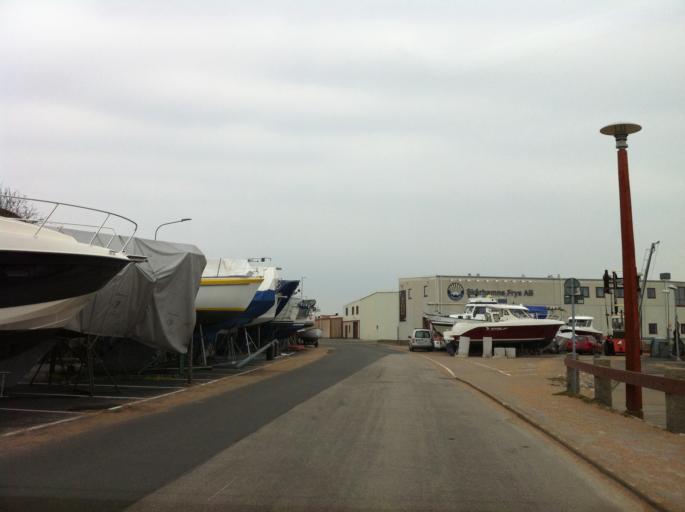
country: SE
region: Vaestra Goetaland
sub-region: Orust
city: Henan
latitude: 58.1505
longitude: 11.7055
